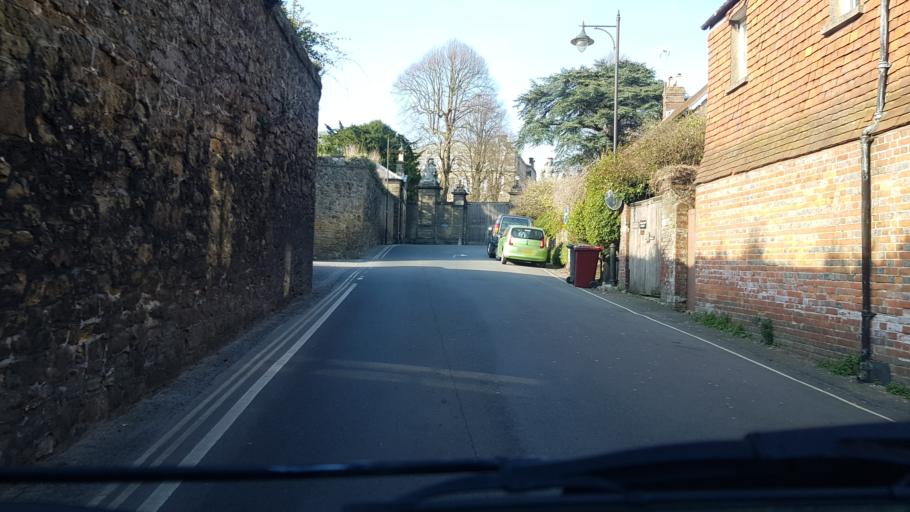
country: GB
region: England
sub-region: West Sussex
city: Petworth
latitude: 50.9864
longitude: -0.6112
